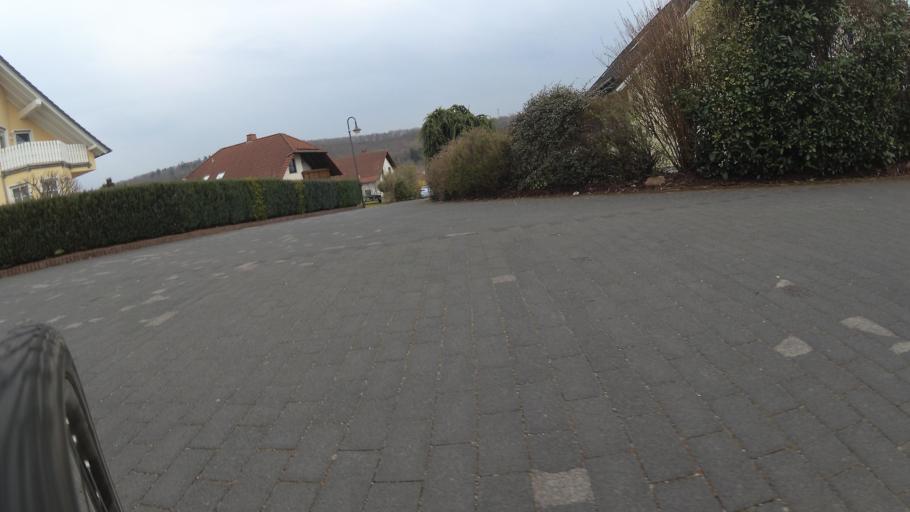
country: DE
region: Rheinland-Pfalz
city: Birkenfeld
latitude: 49.6557
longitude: 7.1738
